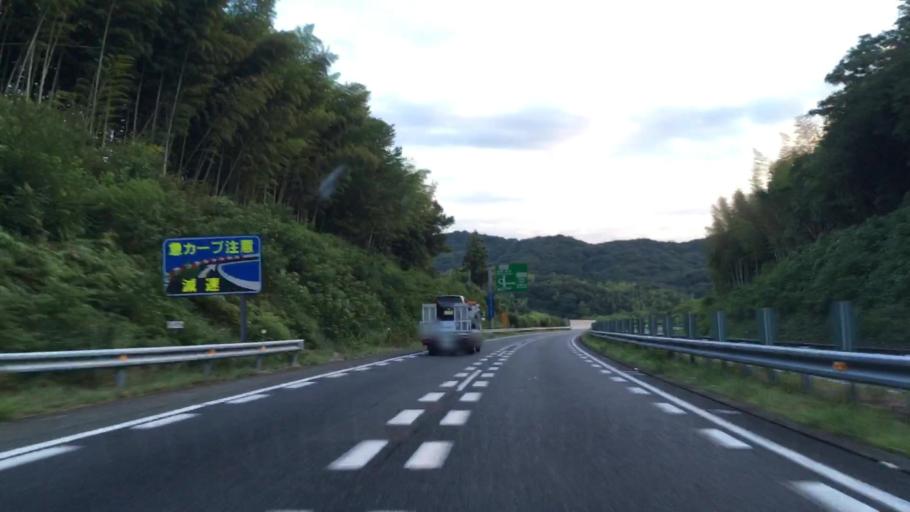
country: JP
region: Yamaguchi
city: Shimonoseki
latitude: 33.9326
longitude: 130.9958
